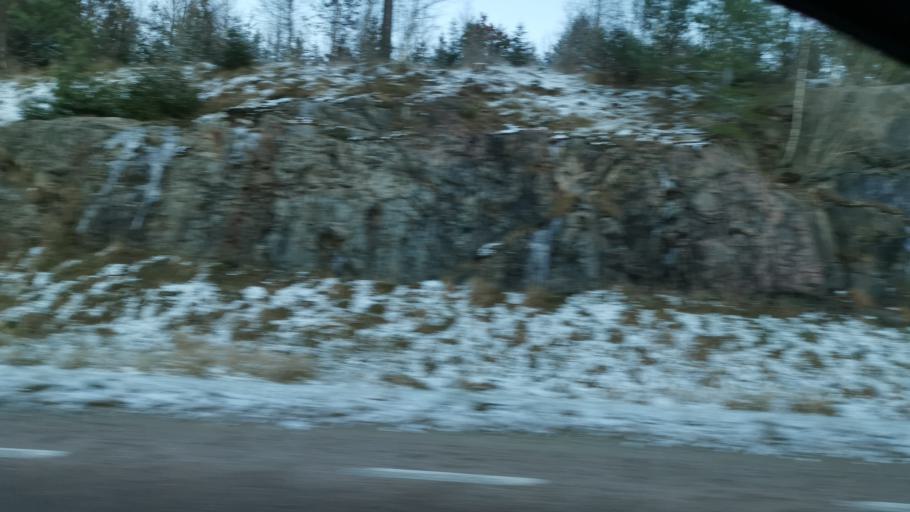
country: SE
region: Vaestra Goetaland
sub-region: Munkedals Kommun
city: Munkedal
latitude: 58.4091
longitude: 11.7362
